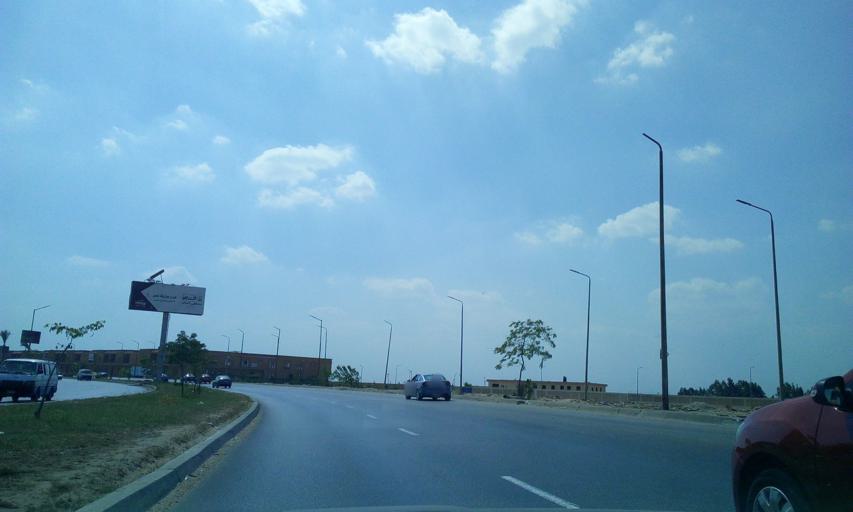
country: EG
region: Muhafazat al Qalyubiyah
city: Al Khankah
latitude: 30.0910
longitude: 31.3708
